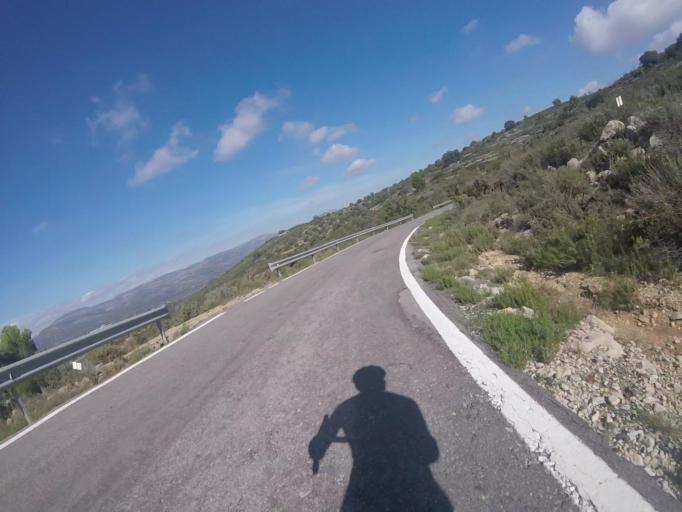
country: ES
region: Valencia
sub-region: Provincia de Castello
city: Albocasser
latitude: 40.3515
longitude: 0.0465
